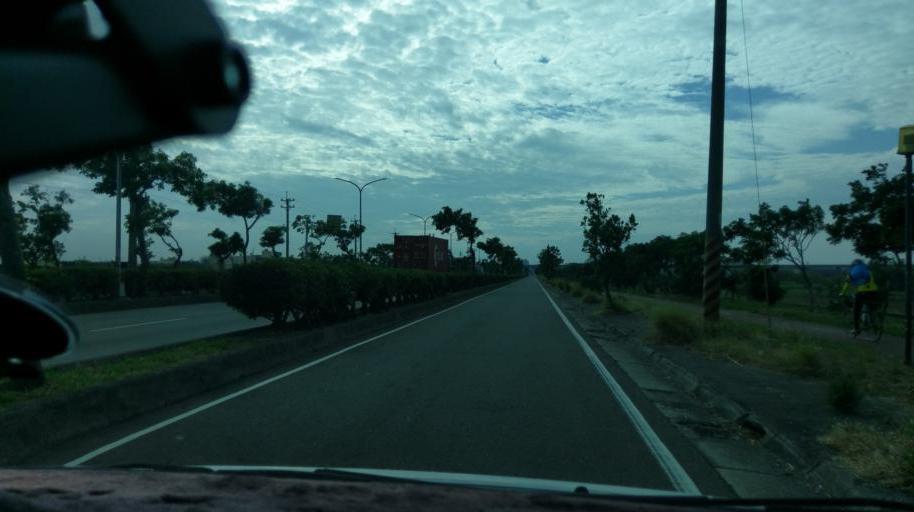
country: TW
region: Taiwan
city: Fengyuan
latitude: 24.2965
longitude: 120.5613
